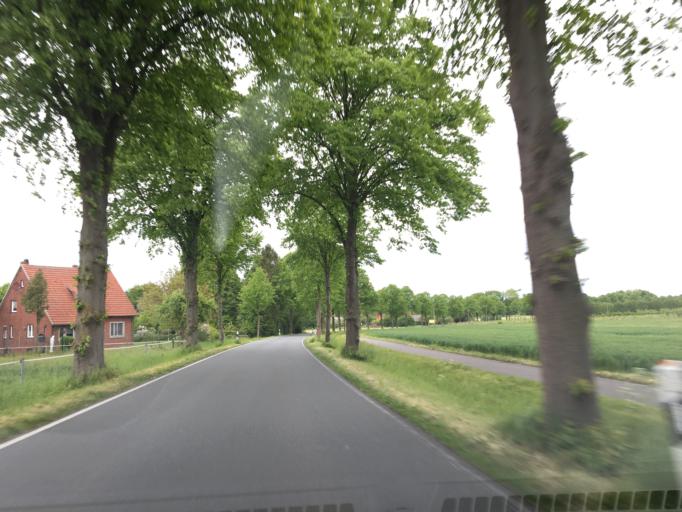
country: DE
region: North Rhine-Westphalia
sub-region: Regierungsbezirk Munster
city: Senden
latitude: 51.9289
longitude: 7.4861
